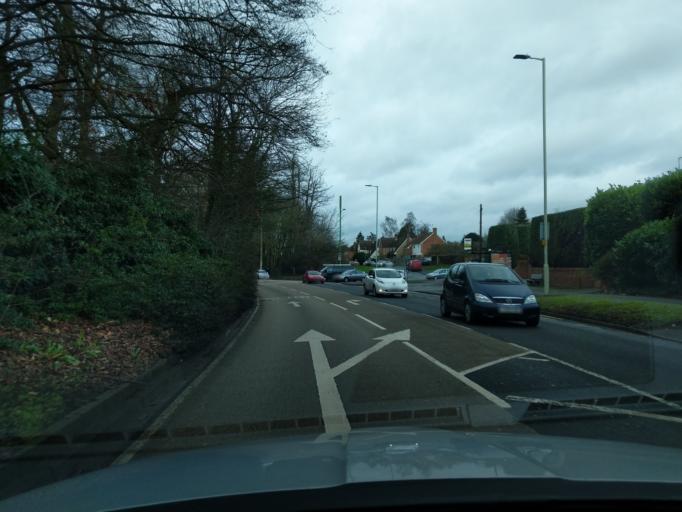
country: GB
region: England
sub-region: Hertfordshire
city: Abbots Langley
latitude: 51.6756
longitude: -0.4207
